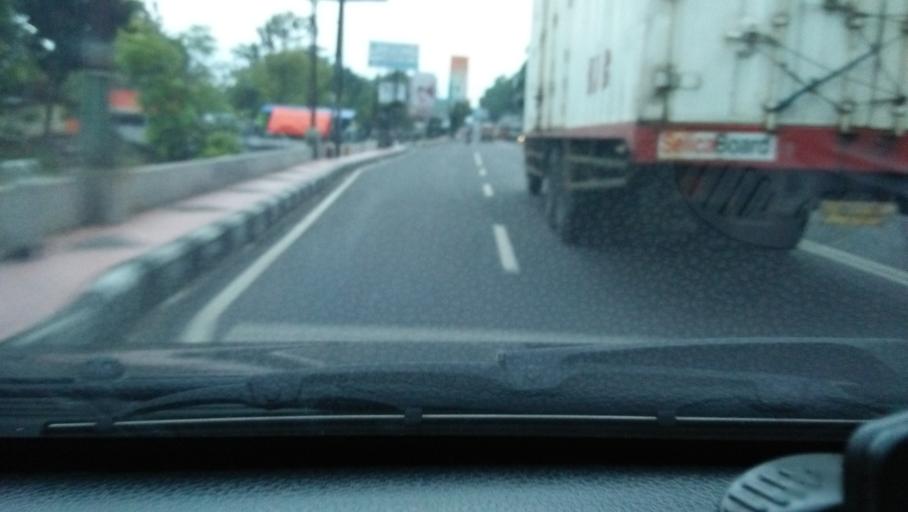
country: ID
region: Central Java
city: Magelang
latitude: -7.4411
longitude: 110.2266
